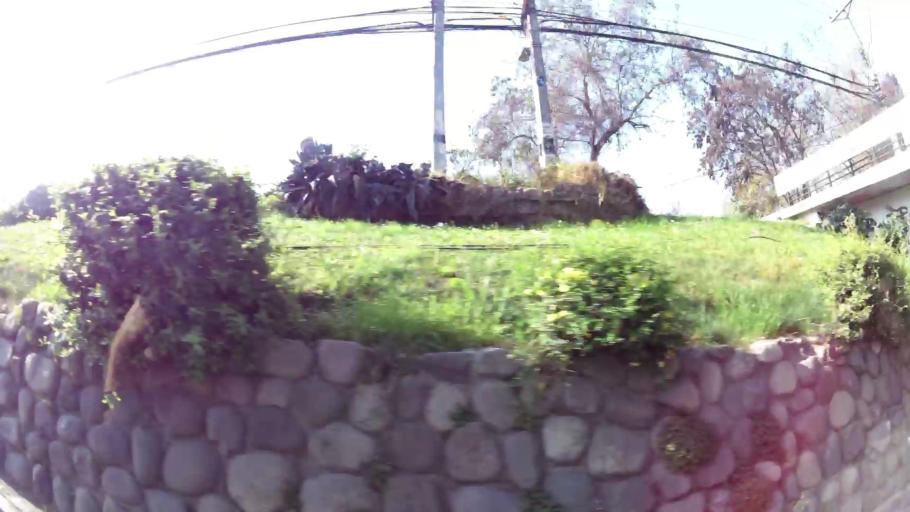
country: CL
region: Santiago Metropolitan
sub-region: Provincia de Santiago
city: Villa Presidente Frei, Nunoa, Santiago, Chile
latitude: -33.4603
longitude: -70.5829
